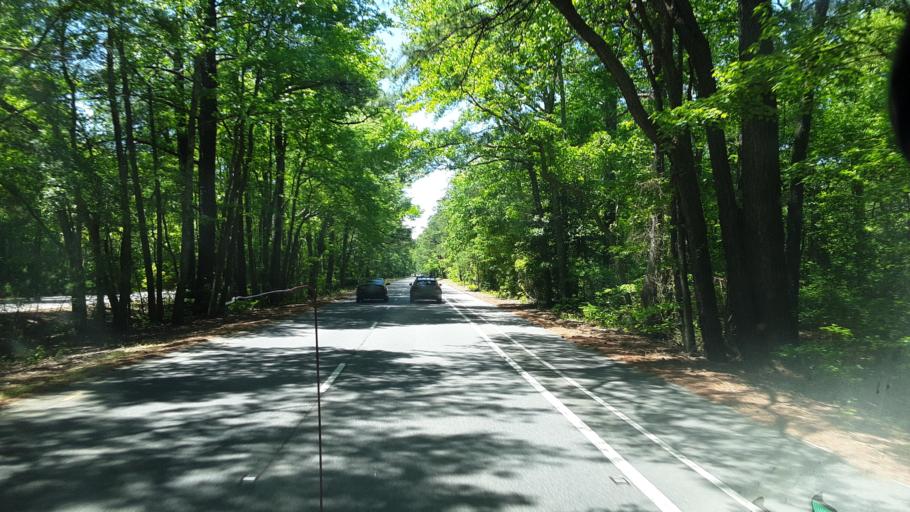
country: US
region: Virginia
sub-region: City of Virginia Beach
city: Virginia Beach
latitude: 36.9200
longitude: -76.0263
